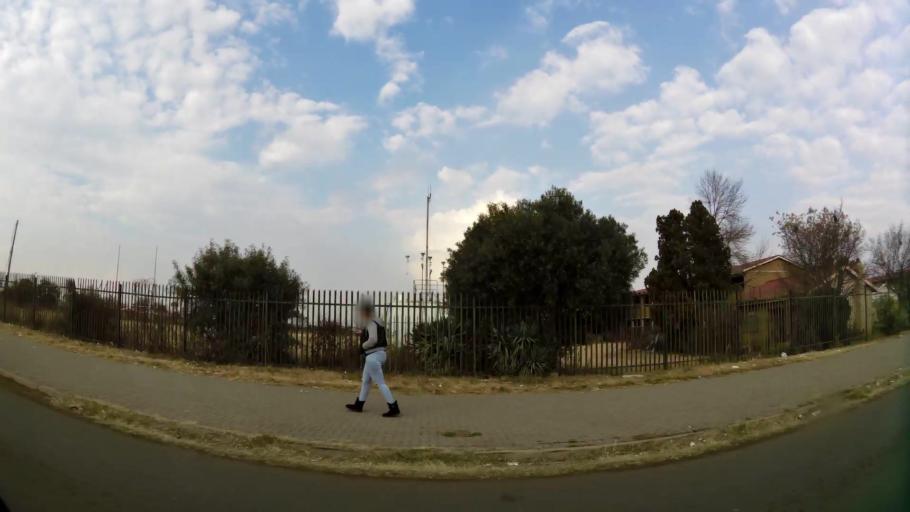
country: ZA
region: Gauteng
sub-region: Sedibeng District Municipality
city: Vanderbijlpark
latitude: -26.6897
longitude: 27.8676
